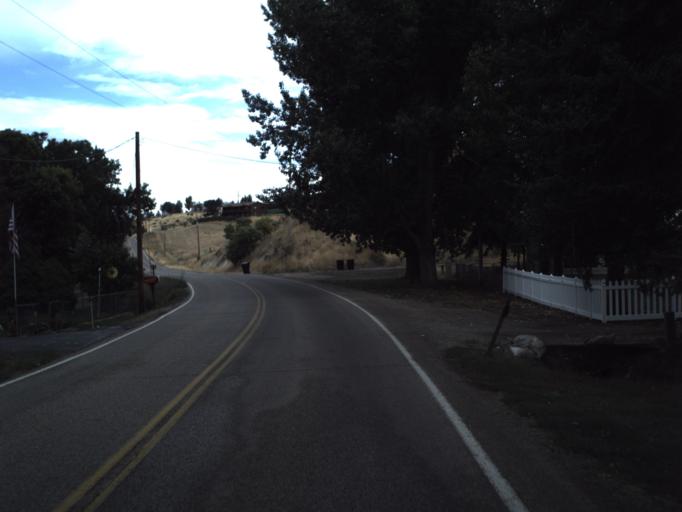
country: US
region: Utah
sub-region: Morgan County
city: Morgan
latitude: 40.9870
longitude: -111.6786
